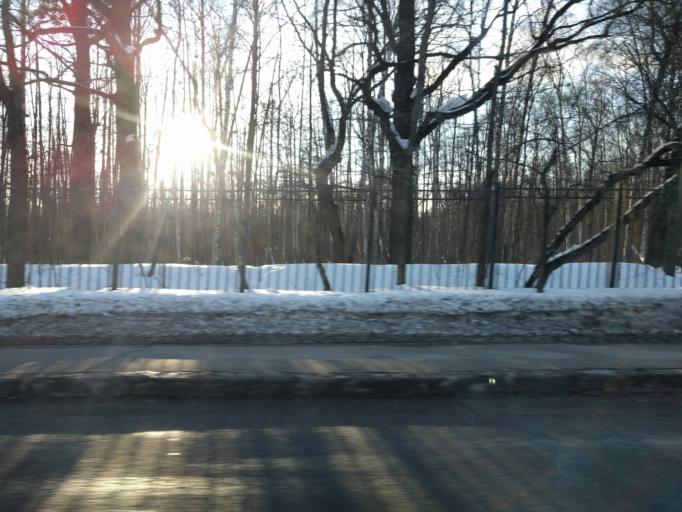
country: RU
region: Moscow
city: Ivanovskoye
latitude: 55.7766
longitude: 37.8194
